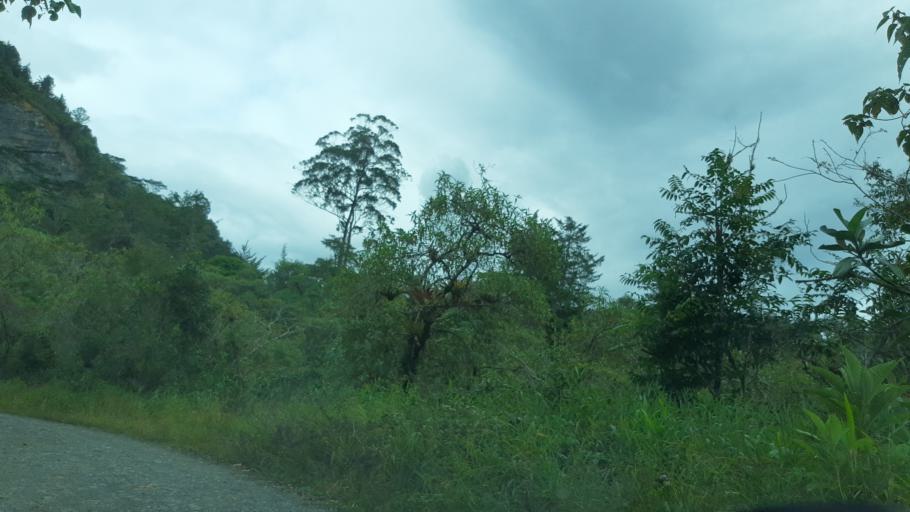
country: CO
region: Boyaca
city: Garagoa
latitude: 5.0399
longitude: -73.3323
